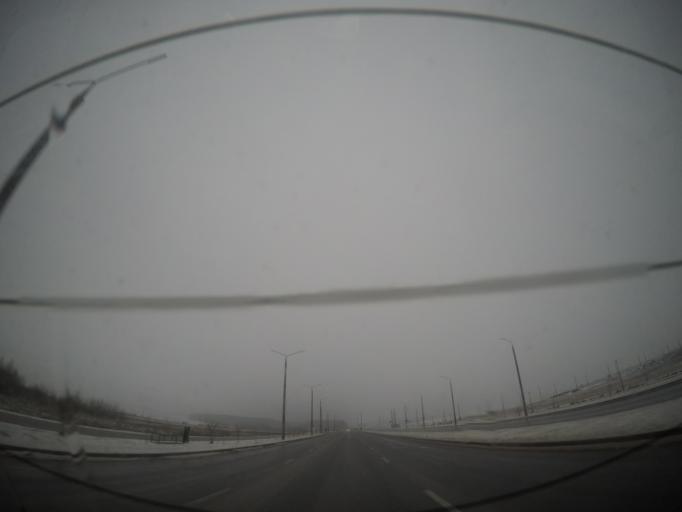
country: BY
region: Grodnenskaya
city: Hrodna
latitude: 53.6124
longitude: 23.8210
